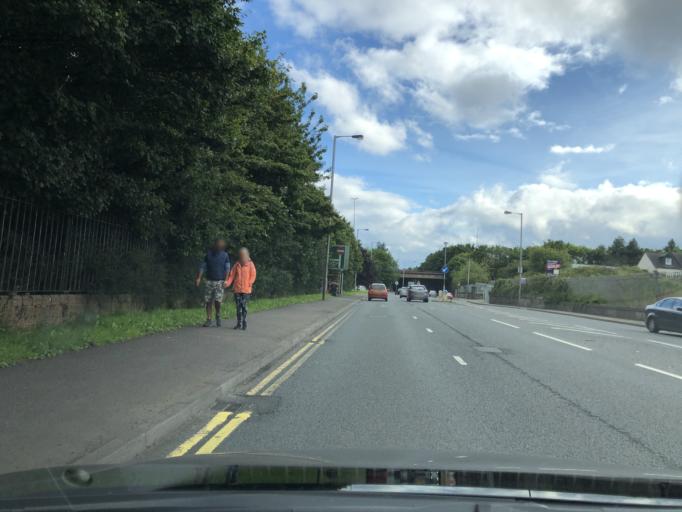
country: GB
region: Northern Ireland
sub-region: Newtownabbey District
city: Newtownabbey
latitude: 54.6505
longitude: -5.9185
